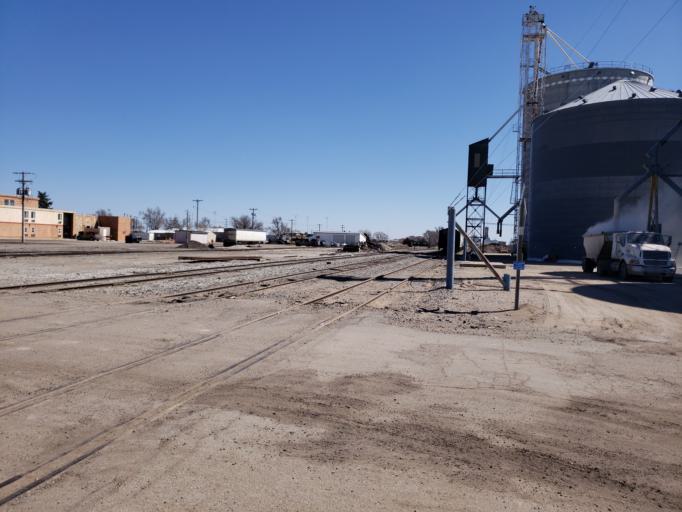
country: US
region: Kansas
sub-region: Ness County
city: Ness City
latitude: 38.4516
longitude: -99.9009
